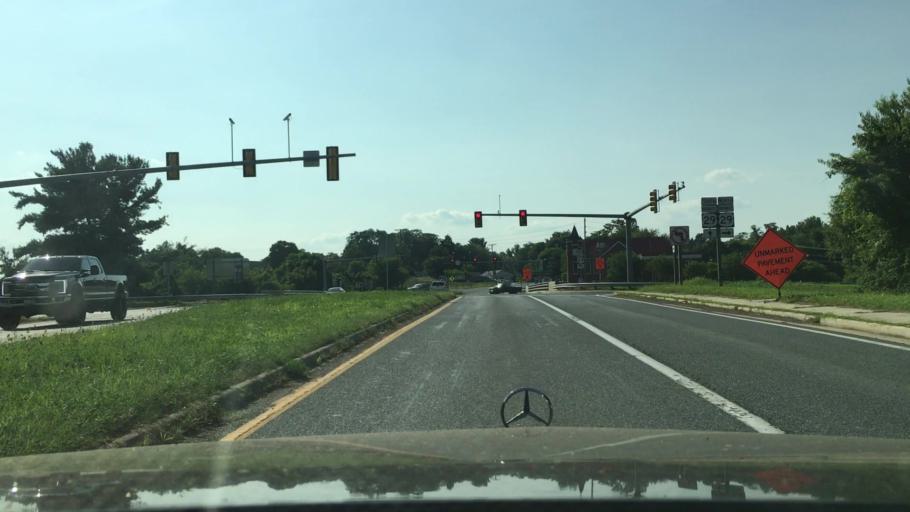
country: US
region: Virginia
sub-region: Amherst County
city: Madison Heights
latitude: 37.4216
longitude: -79.1218
